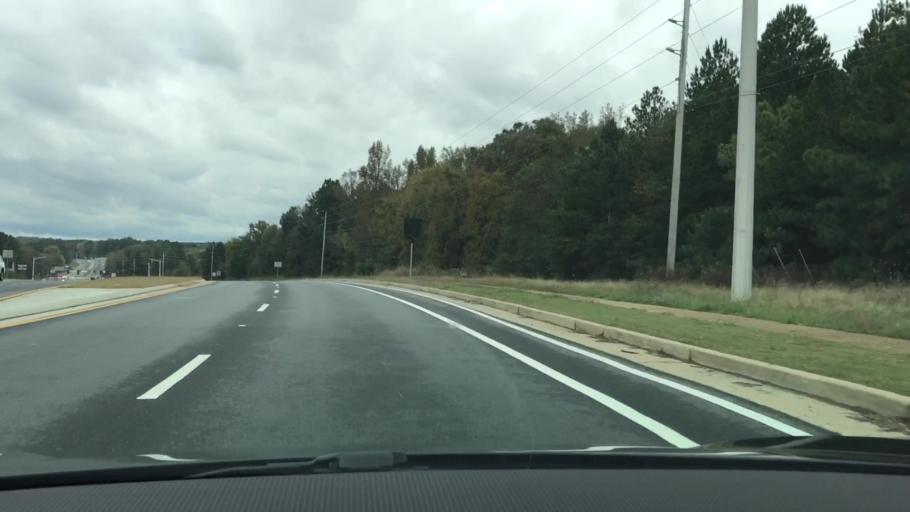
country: US
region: Georgia
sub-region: Oconee County
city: Watkinsville
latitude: 33.9102
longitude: -83.4655
